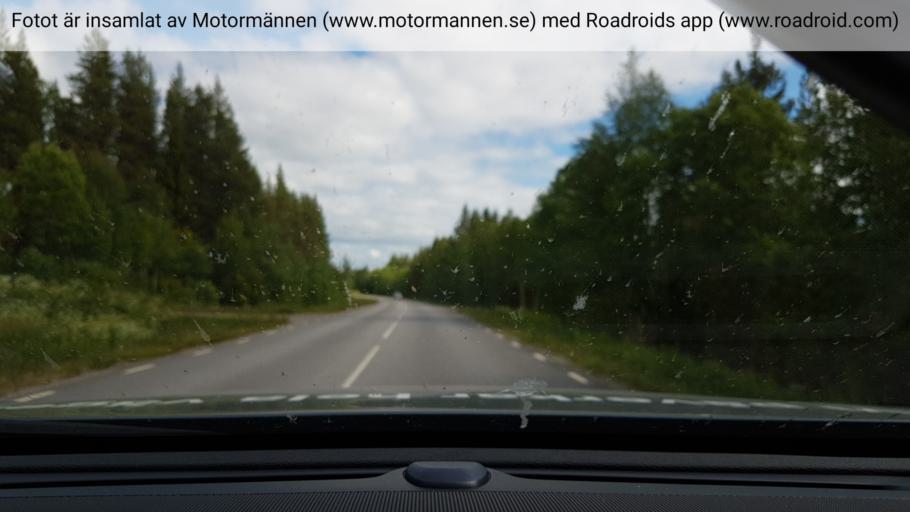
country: SE
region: Vaesterbotten
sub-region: Sorsele Kommun
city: Sorsele
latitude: 65.6887
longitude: 17.2027
